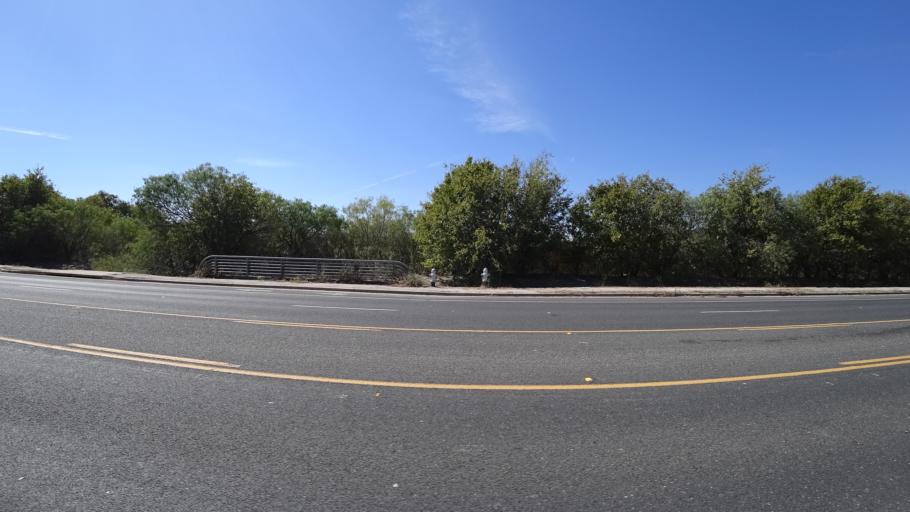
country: US
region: Texas
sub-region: Travis County
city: Austin
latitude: 30.1897
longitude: -97.6960
